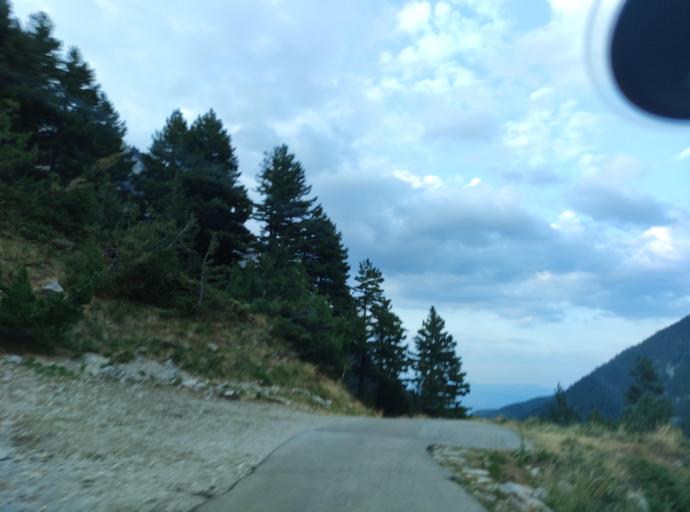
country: BG
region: Blagoevgrad
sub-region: Obshtina Bansko
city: Bansko
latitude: 41.7627
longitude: 23.4180
